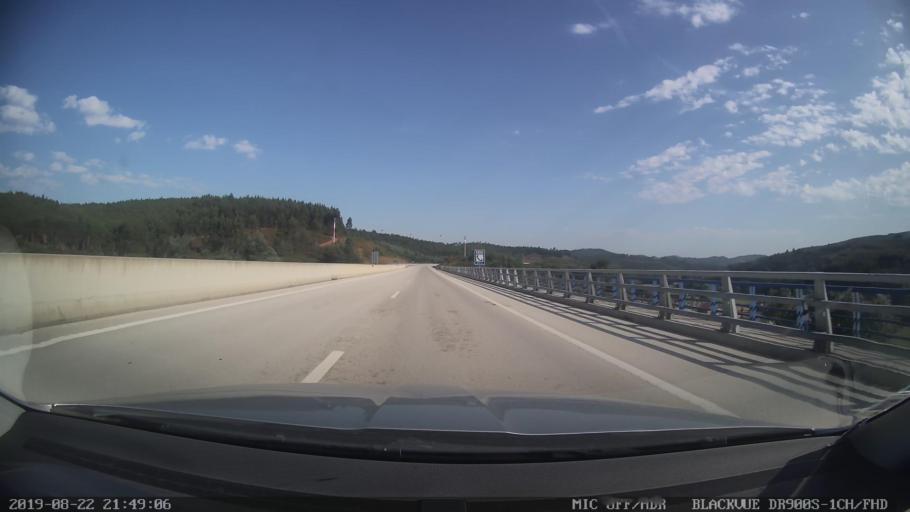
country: PT
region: Coimbra
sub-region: Penela
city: Penela
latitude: 40.0382
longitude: -8.3735
